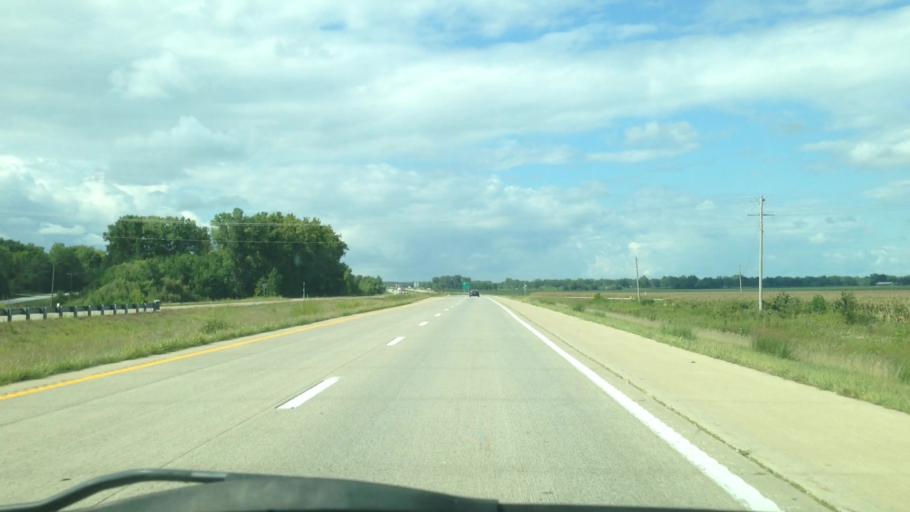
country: US
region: Illinois
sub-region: Hancock County
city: Warsaw
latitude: 40.3443
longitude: -91.5867
